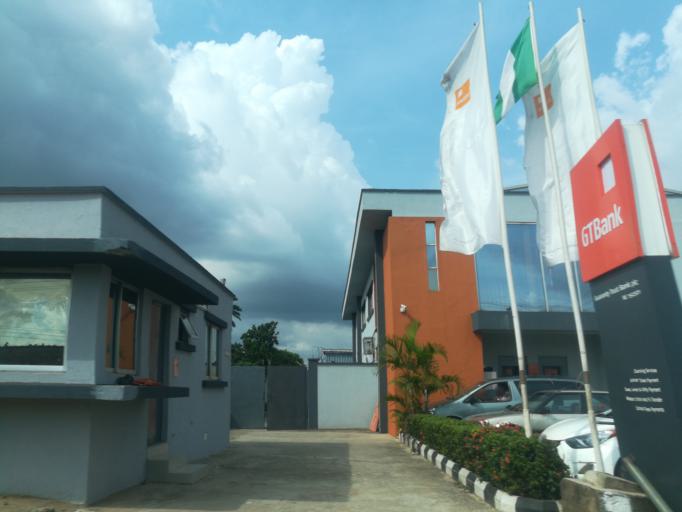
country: NG
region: Oyo
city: Ibadan
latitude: 7.3833
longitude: 3.8323
